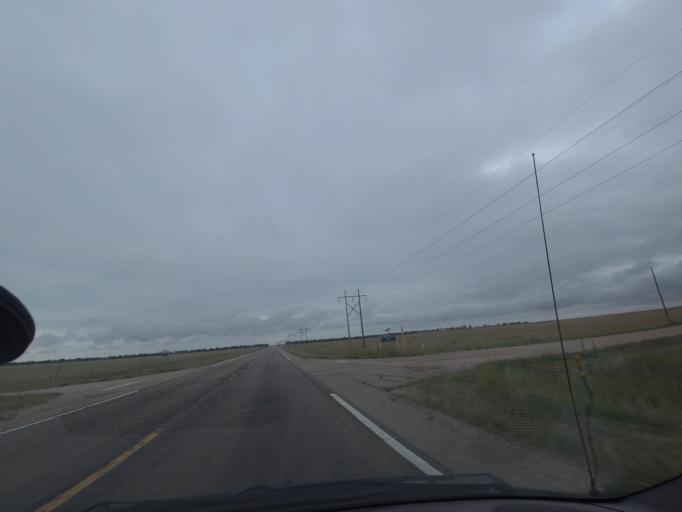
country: US
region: Colorado
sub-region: Yuma County
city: Yuma
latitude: 39.6554
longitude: -102.7645
